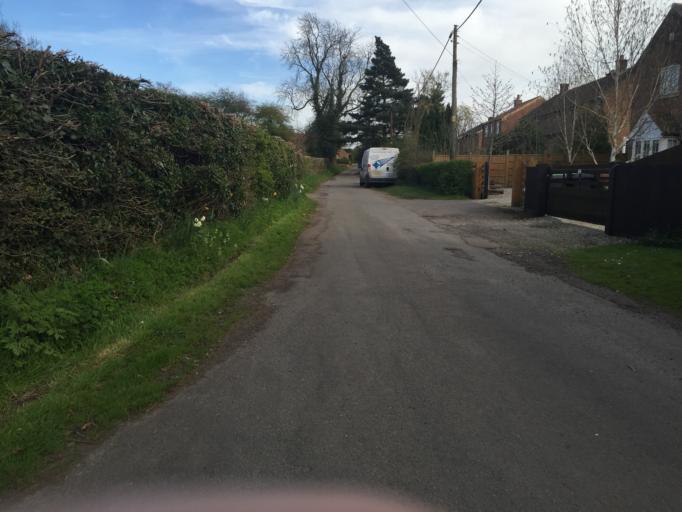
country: GB
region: England
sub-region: Lincolnshire
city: Skellingthorpe
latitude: 53.1259
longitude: -0.6440
